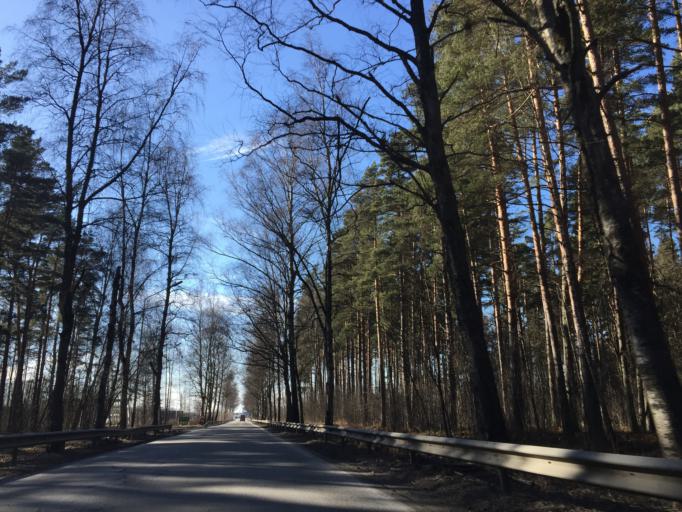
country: LV
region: Babite
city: Pinki
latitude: 56.9559
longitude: 23.9226
